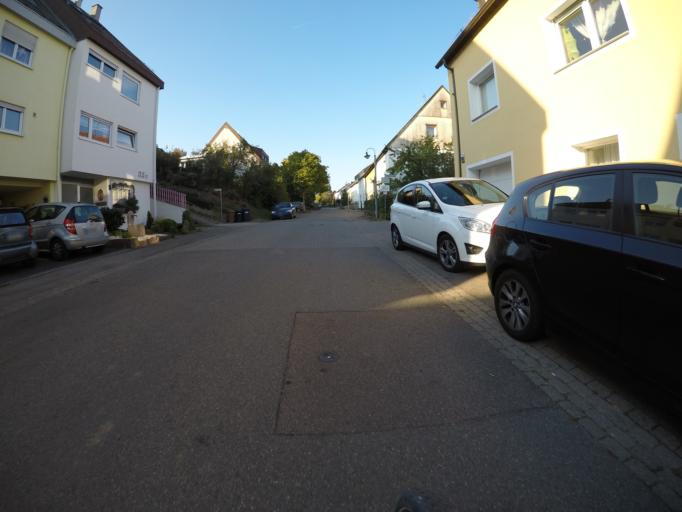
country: DE
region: Baden-Wuerttemberg
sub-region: Regierungsbezirk Stuttgart
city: Ostfildern
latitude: 48.7190
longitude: 9.2351
